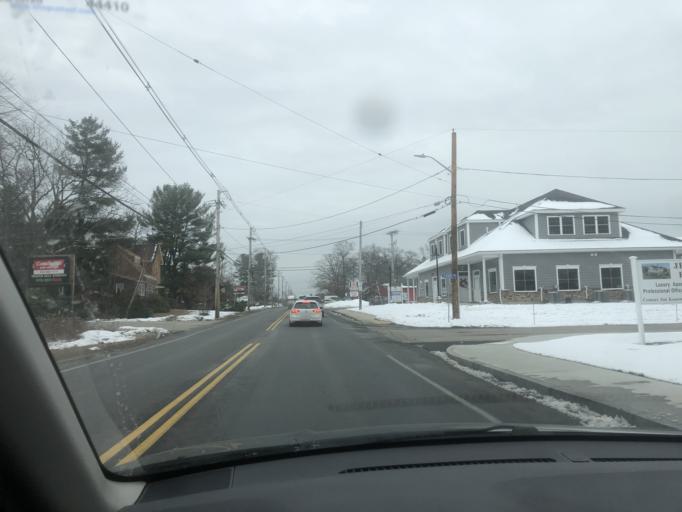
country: US
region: Massachusetts
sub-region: Middlesex County
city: Tewksbury
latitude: 42.6164
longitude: -71.2453
